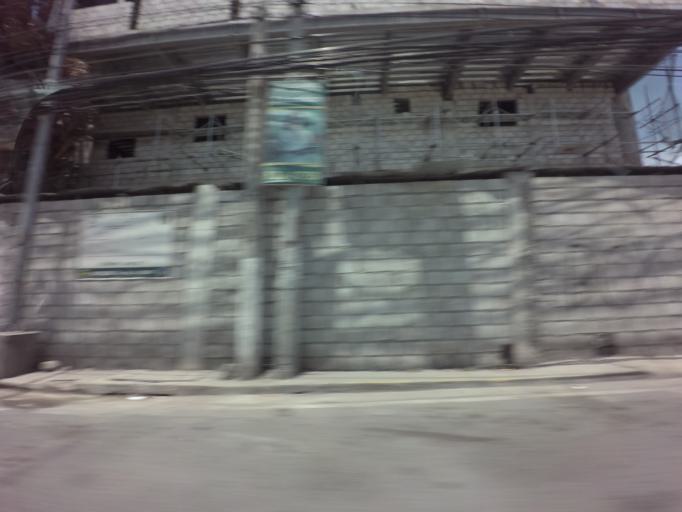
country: PH
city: Sambayanihan People's Village
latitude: 14.4900
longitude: 120.9871
